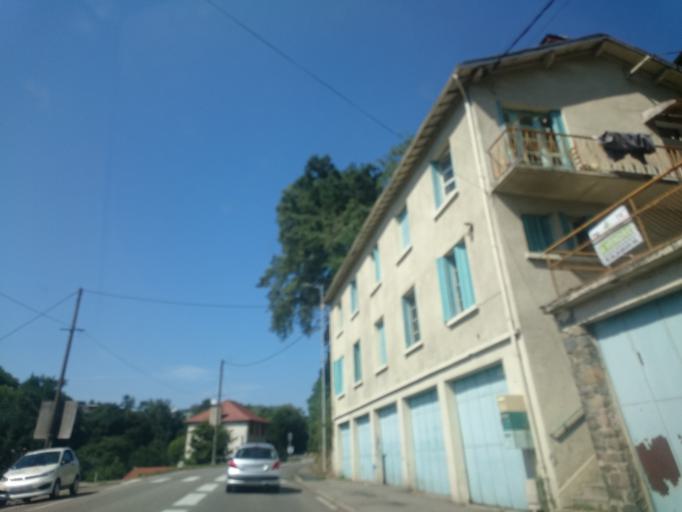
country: FR
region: Limousin
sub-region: Departement de la Correze
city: Tulle
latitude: 45.2806
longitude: 1.7690
